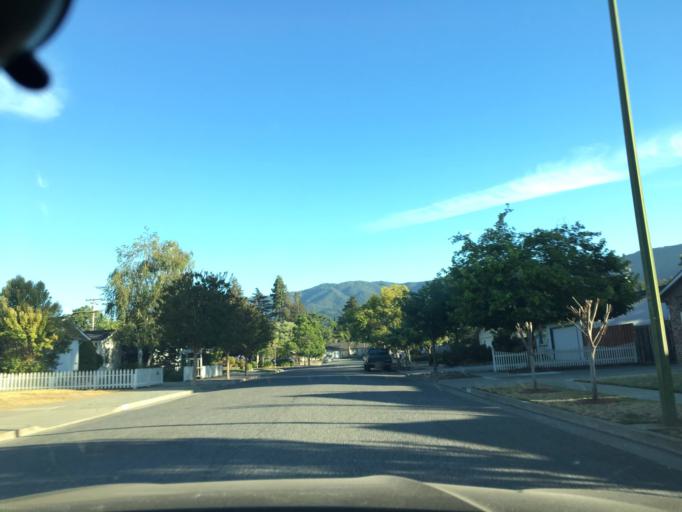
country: US
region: California
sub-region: Santa Clara County
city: Cambrian Park
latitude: 37.2342
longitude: -121.9079
